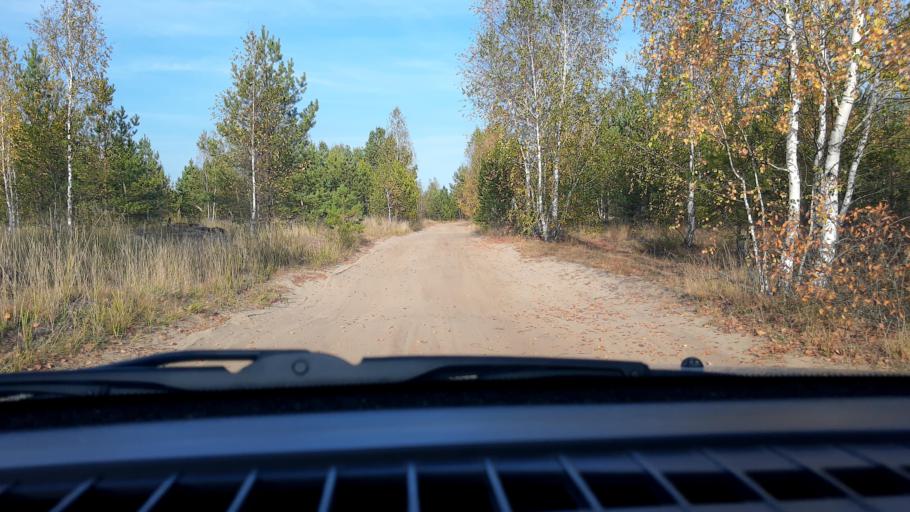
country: RU
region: Nizjnij Novgorod
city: Lukino
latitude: 56.3898
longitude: 43.5993
